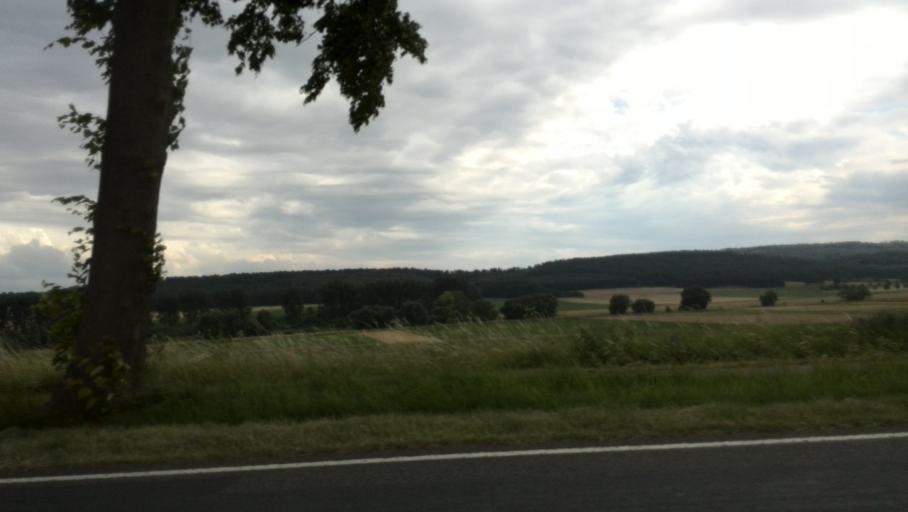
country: DE
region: Lower Saxony
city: Holle
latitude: 52.1064
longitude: 10.1142
